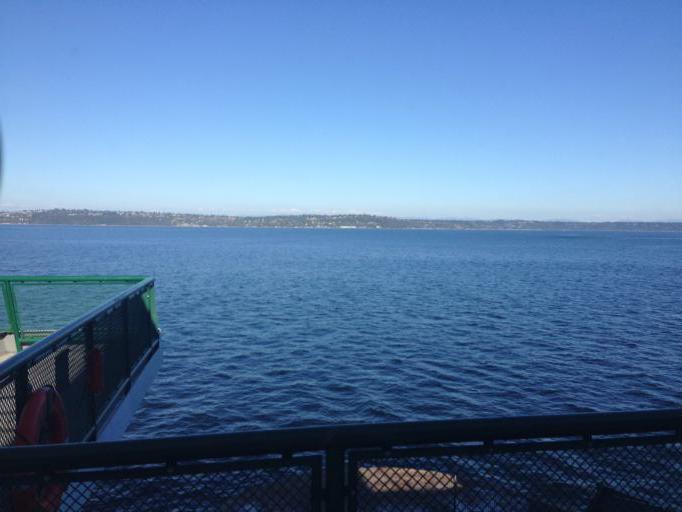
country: US
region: Washington
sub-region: Kitsap County
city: Southworth
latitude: 47.5163
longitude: -122.4730
